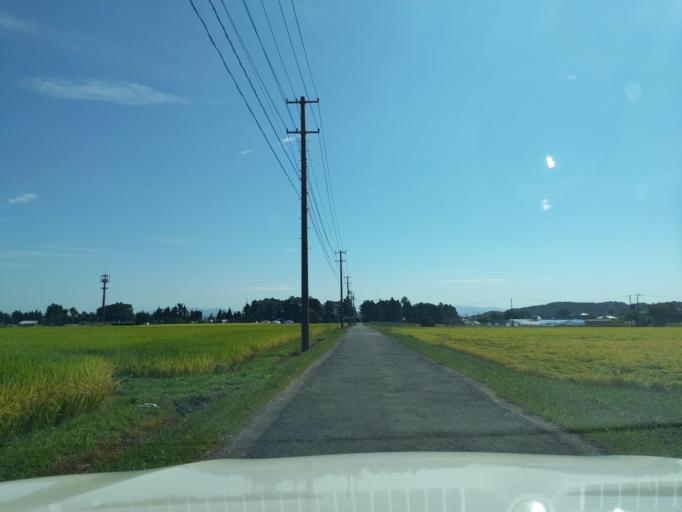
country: JP
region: Fukushima
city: Koriyama
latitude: 37.4005
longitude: 140.2638
